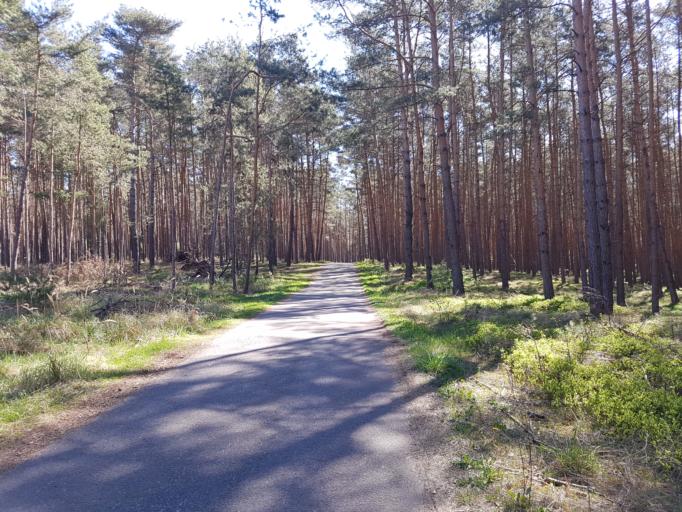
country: DE
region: Brandenburg
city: Groden
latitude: 51.3863
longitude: 13.5659
